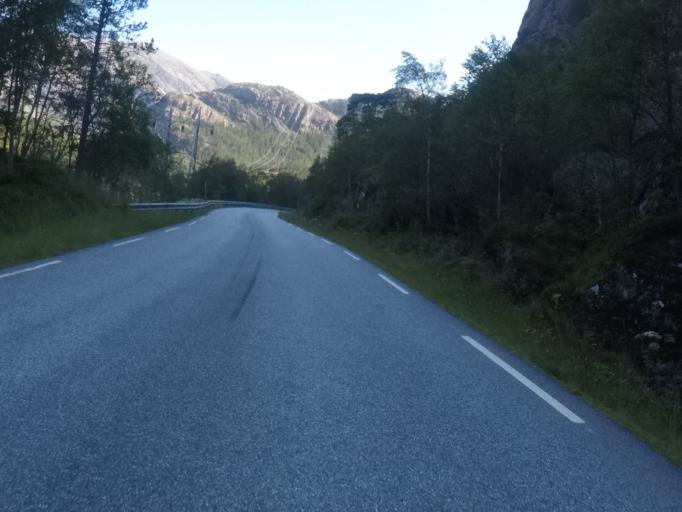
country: NO
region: Sogn og Fjordane
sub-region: Bremanger
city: Svelgen
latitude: 61.7779
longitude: 5.3300
